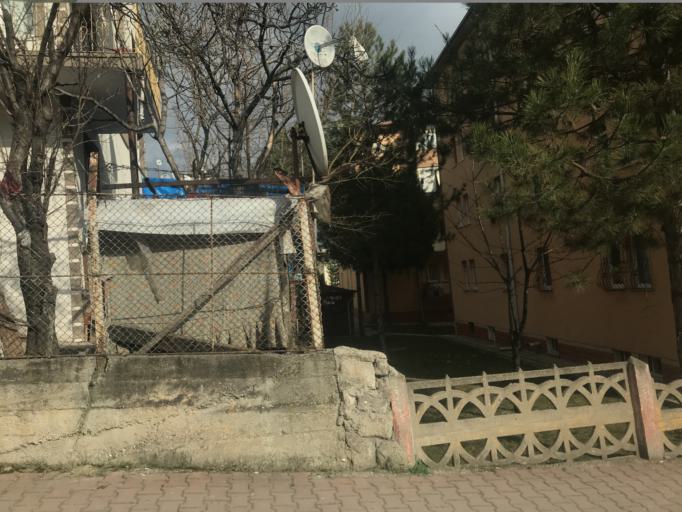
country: TR
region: Karabuk
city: Safranbolu
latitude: 41.2536
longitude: 32.6828
